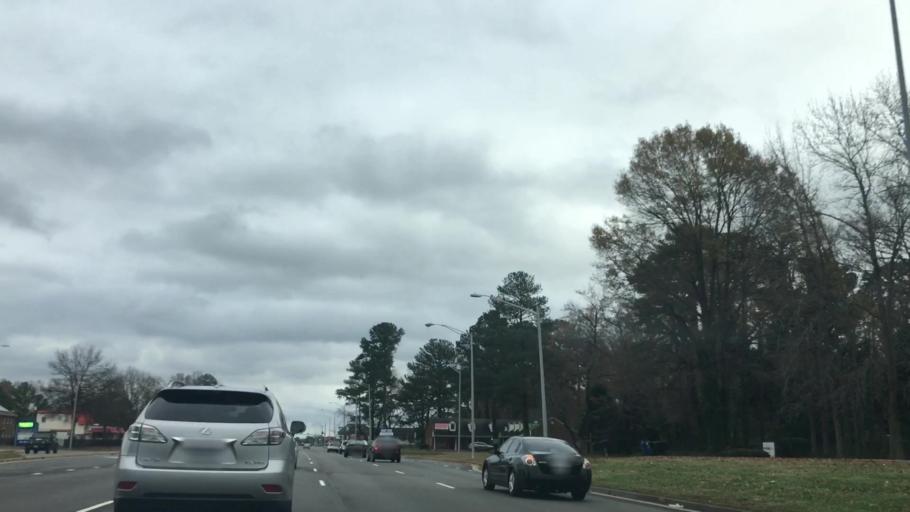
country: US
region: Virginia
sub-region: City of Chesapeake
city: Chesapeake
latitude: 36.8288
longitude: -76.1351
